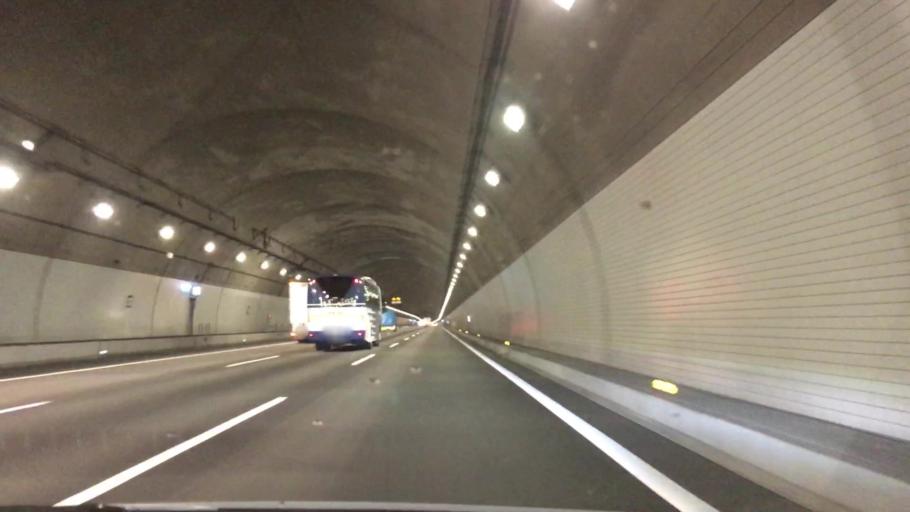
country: JP
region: Shizuoka
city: Fujieda
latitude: 34.9552
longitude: 138.2856
